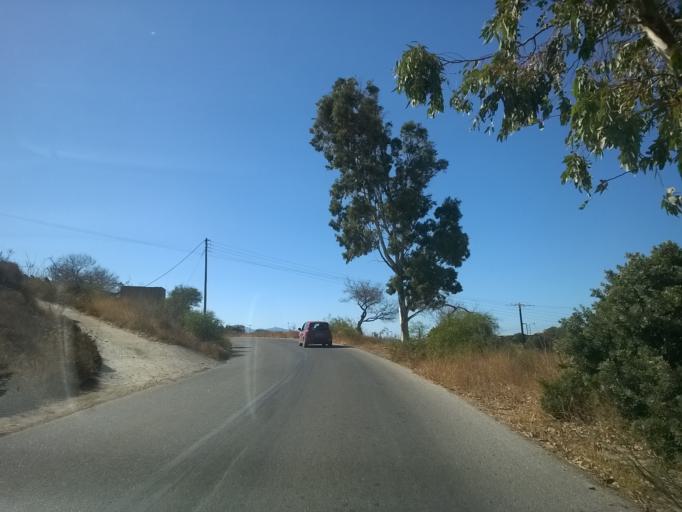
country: GR
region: South Aegean
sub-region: Nomos Kykladon
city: Naxos
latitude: 37.0432
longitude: 25.4094
